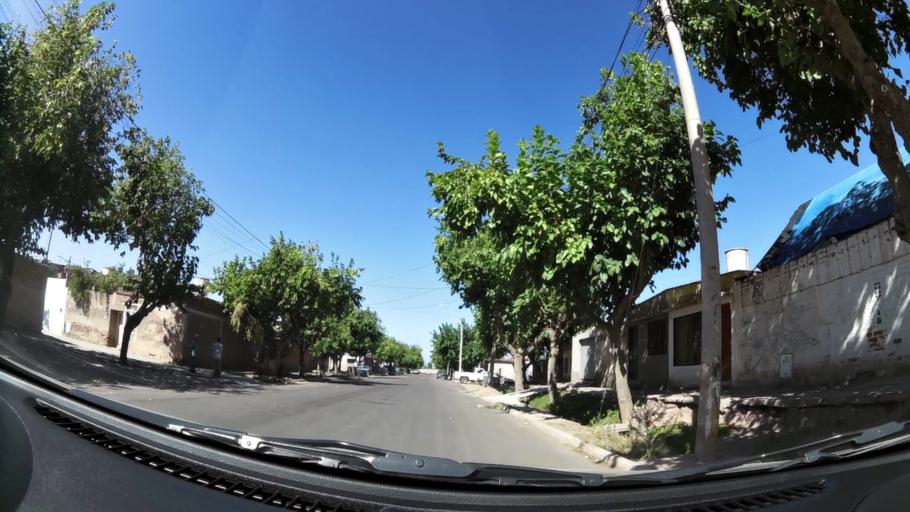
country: AR
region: Mendoza
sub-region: Departamento de Godoy Cruz
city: Godoy Cruz
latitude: -32.9571
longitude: -68.8310
